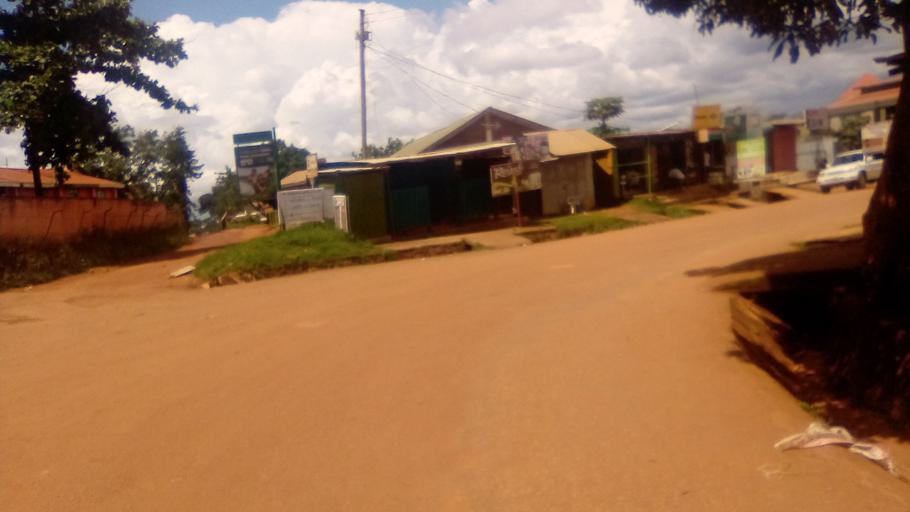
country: UG
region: Central Region
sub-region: Wakiso District
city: Entebbe
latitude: 0.0966
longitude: 32.5062
